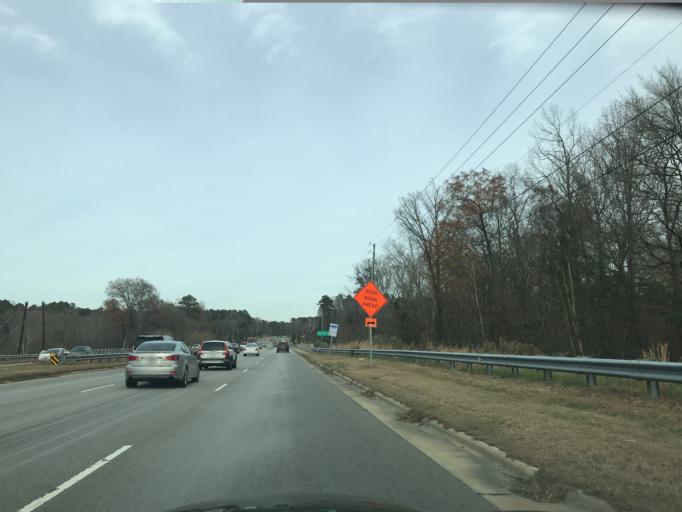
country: US
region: North Carolina
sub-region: Wake County
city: Rolesville
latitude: 35.8832
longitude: -78.5289
